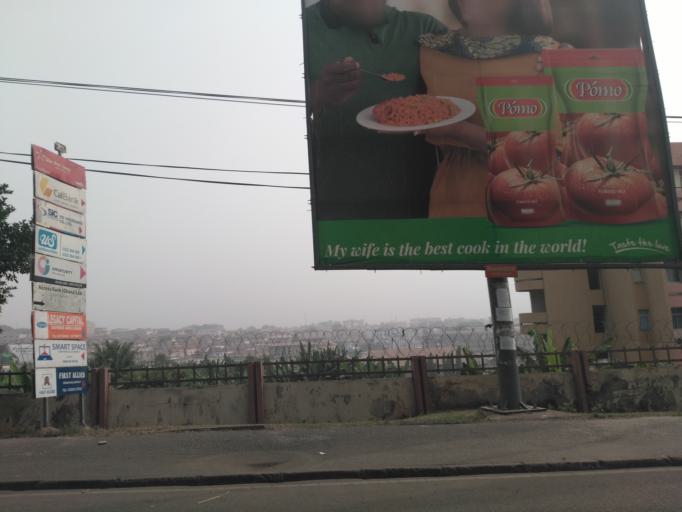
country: GH
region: Ashanti
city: Kumasi
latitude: 6.6877
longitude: -1.6185
